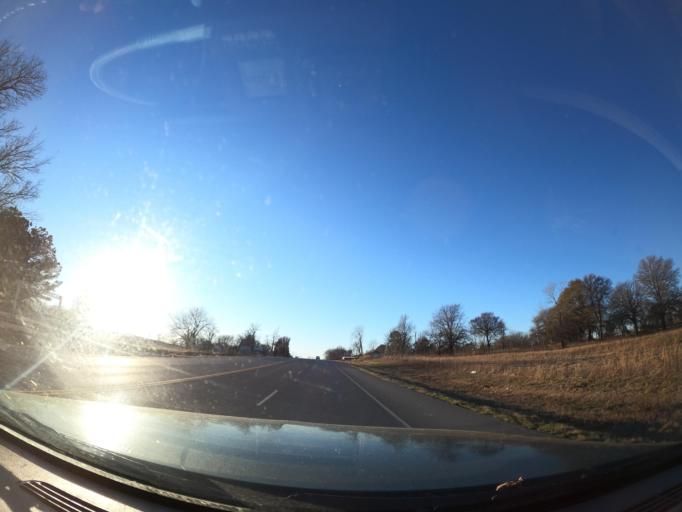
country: US
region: Oklahoma
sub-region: Pittsburg County
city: Krebs
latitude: 34.8942
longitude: -95.6461
